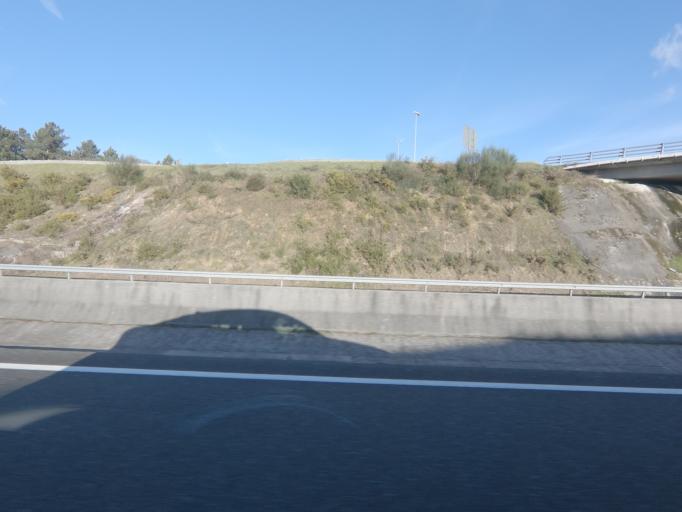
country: ES
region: Galicia
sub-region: Provincia de Pontevedra
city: Lalin
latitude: 42.6387
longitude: -8.1322
